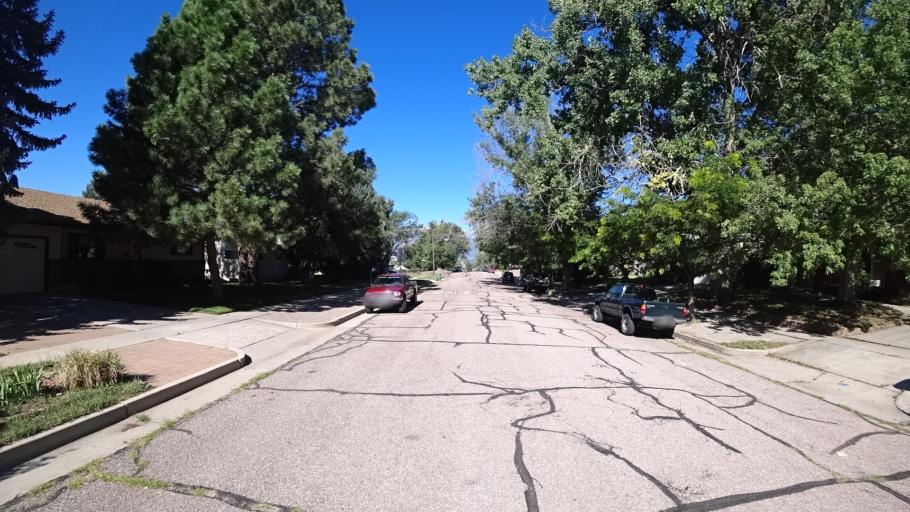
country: US
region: Colorado
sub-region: El Paso County
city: Colorado Springs
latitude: 38.8584
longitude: -104.7840
